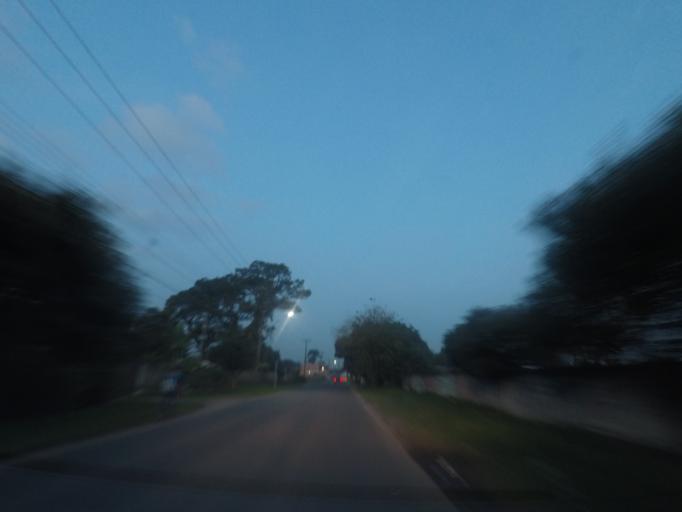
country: BR
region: Parana
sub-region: Pinhais
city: Pinhais
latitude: -25.4592
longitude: -49.1583
